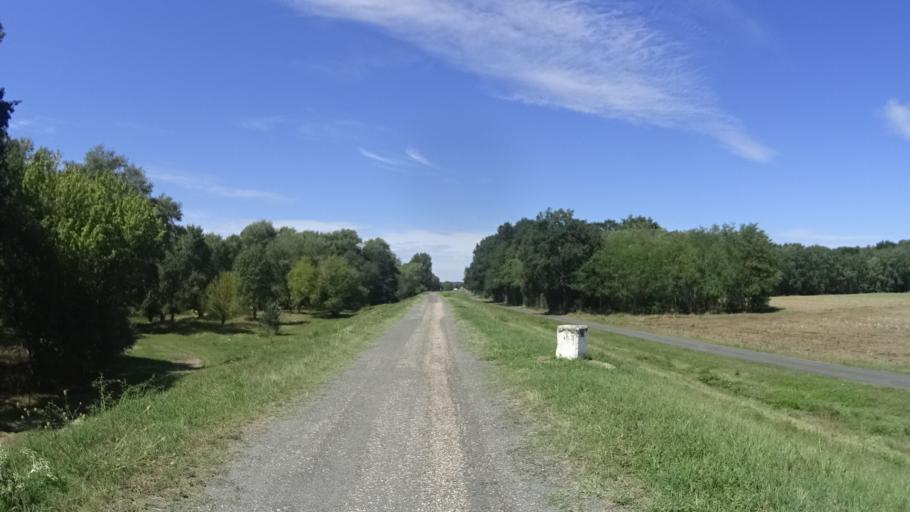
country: FR
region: Centre
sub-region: Departement du Loiret
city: Briare
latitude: 47.5932
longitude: 2.7733
